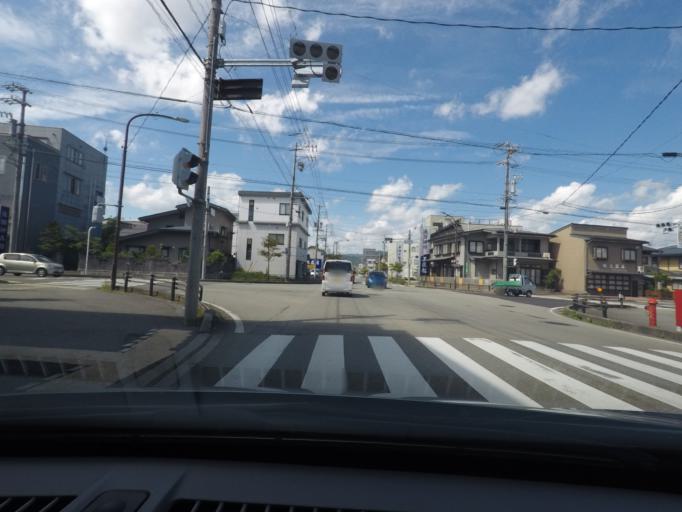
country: JP
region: Gifu
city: Takayama
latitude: 36.1532
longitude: 137.2546
